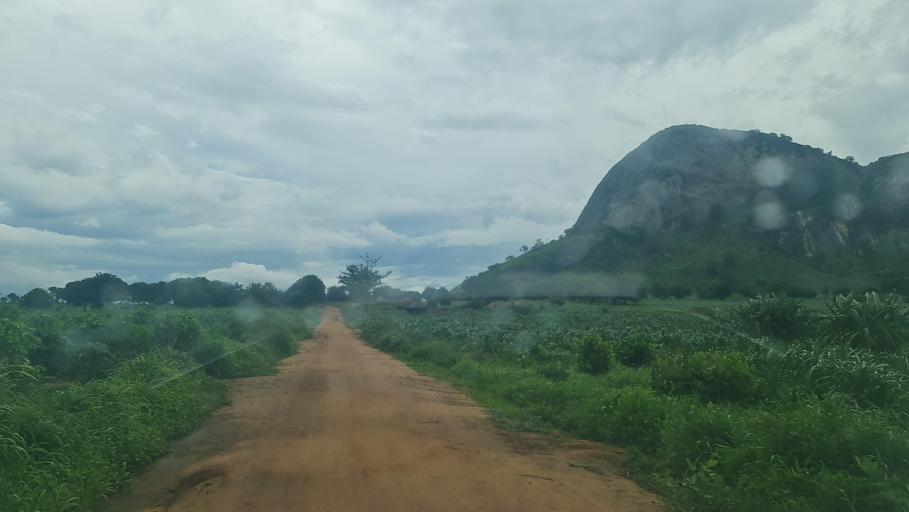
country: MW
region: Southern Region
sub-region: Nsanje District
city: Nsanje
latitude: -17.3971
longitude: 35.5840
